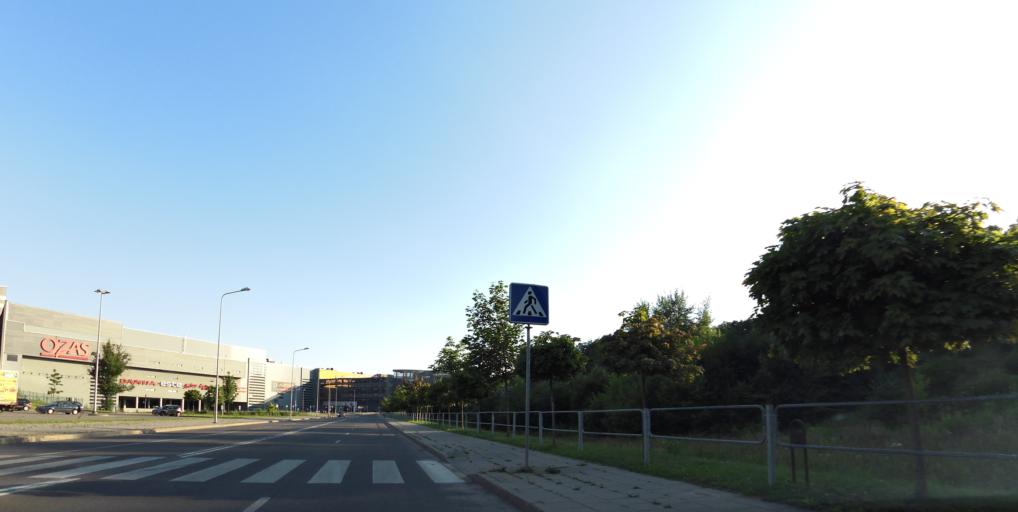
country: LT
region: Vilnius County
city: Seskine
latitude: 54.7174
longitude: 25.2752
